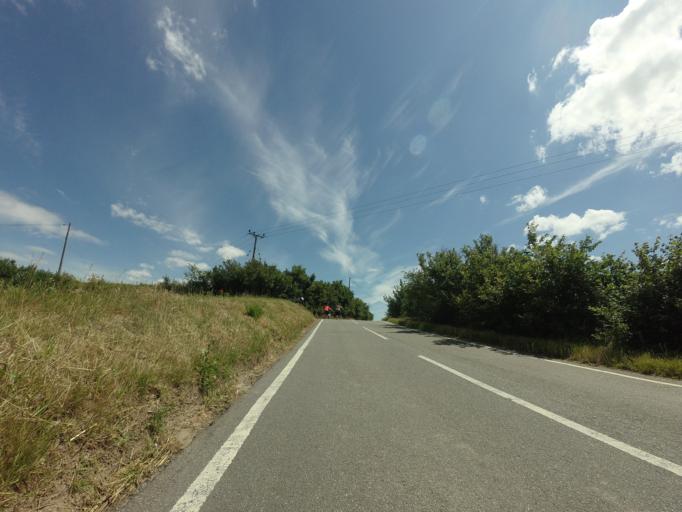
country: GB
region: England
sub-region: Medway
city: High Halstow
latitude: 51.4510
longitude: 0.5492
